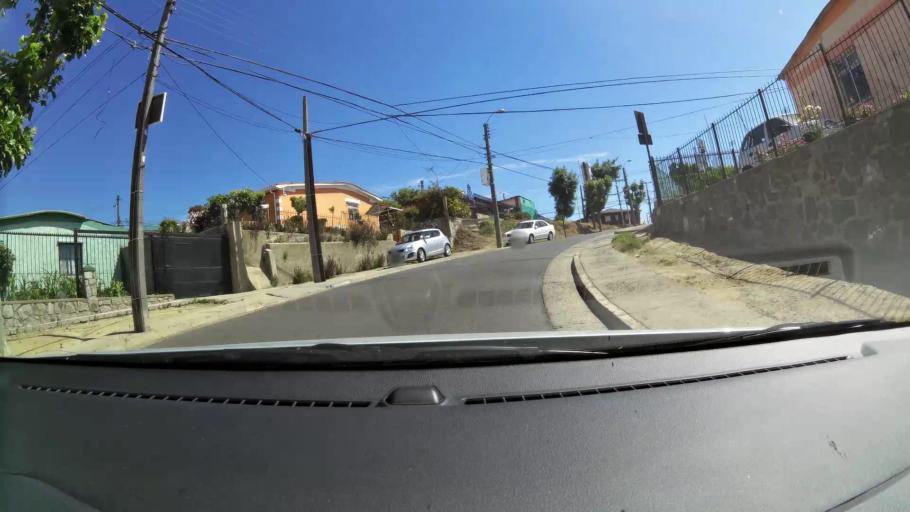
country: CL
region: Valparaiso
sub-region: Provincia de Valparaiso
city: Vina del Mar
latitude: -33.0410
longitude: -71.5769
